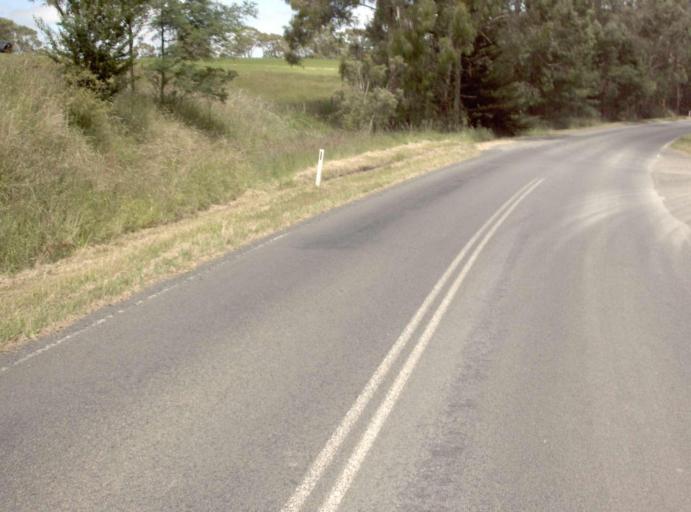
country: AU
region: Victoria
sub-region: Baw Baw
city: Warragul
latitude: -38.4905
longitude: 145.9985
